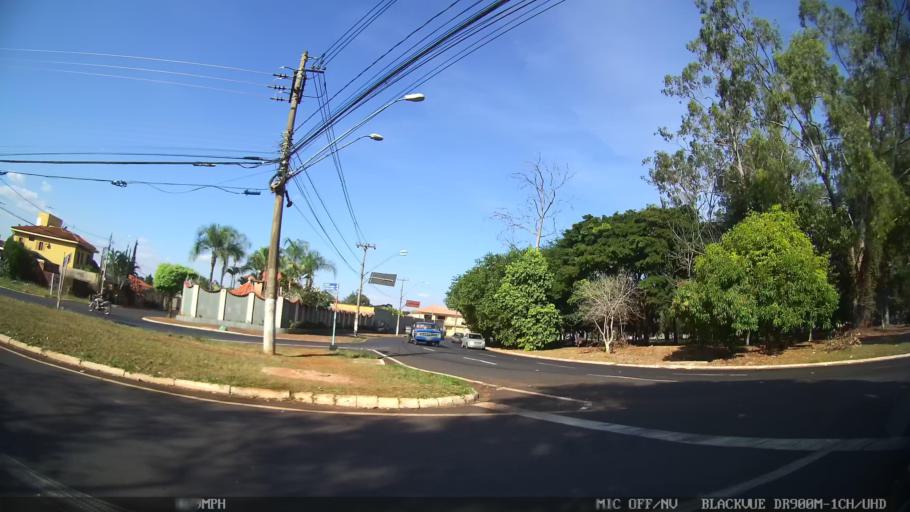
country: BR
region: Sao Paulo
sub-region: Ribeirao Preto
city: Ribeirao Preto
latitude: -21.1923
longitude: -47.7610
